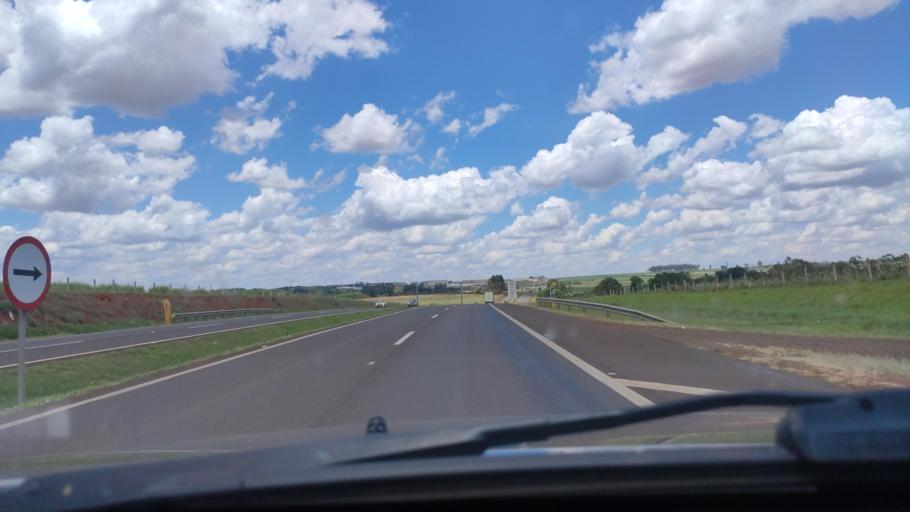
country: BR
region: Sao Paulo
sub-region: Pederneiras
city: Pederneiras
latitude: -22.3274
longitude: -48.7420
